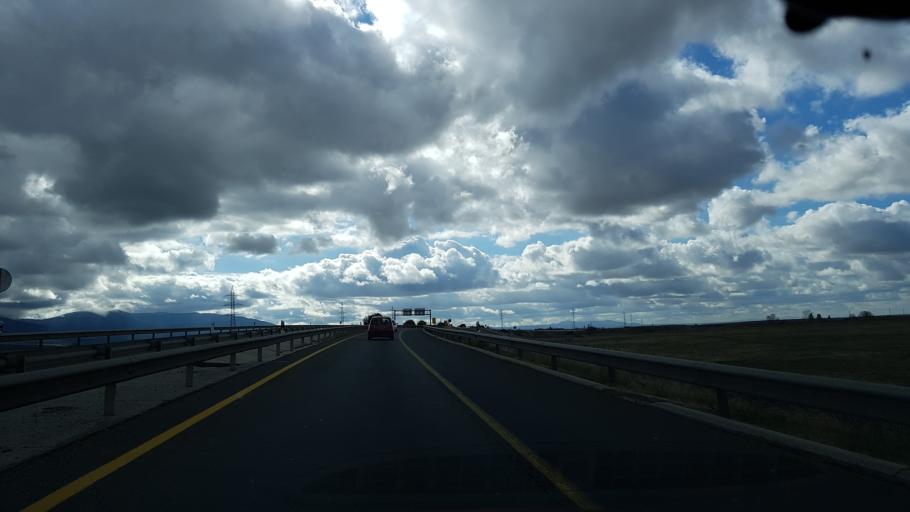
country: ES
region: Castille and Leon
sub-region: Provincia de Segovia
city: Palazuelos de Eresma
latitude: 40.9264
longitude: -4.0878
